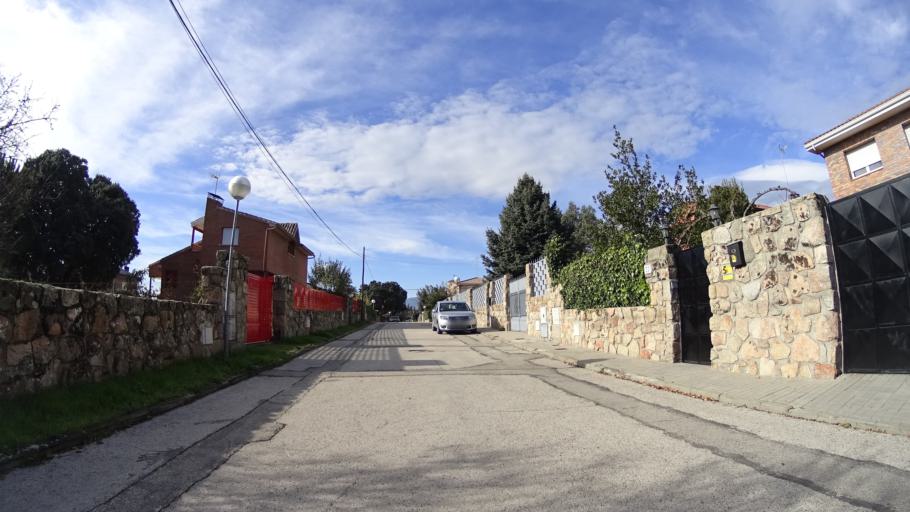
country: ES
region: Madrid
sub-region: Provincia de Madrid
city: Galapagar
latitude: 40.5801
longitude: -4.0181
